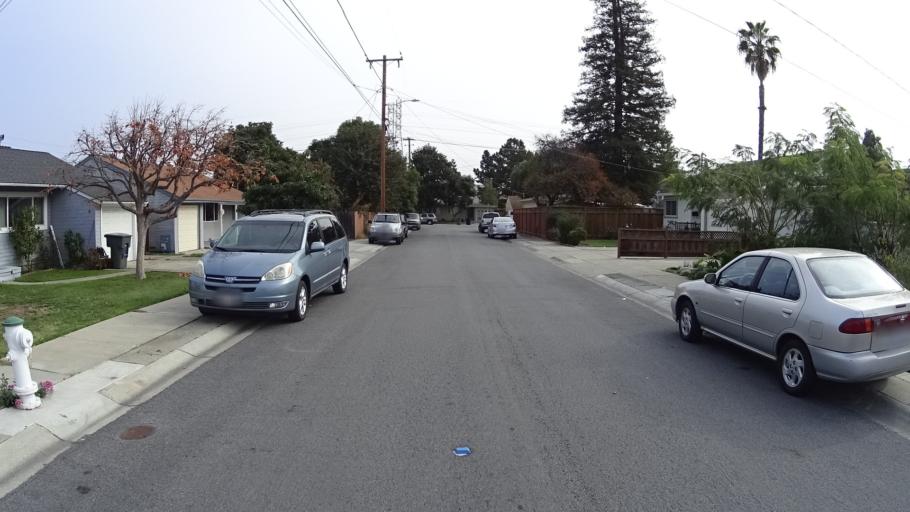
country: US
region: California
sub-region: Santa Clara County
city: Sunnyvale
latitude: 37.3786
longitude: -122.0172
